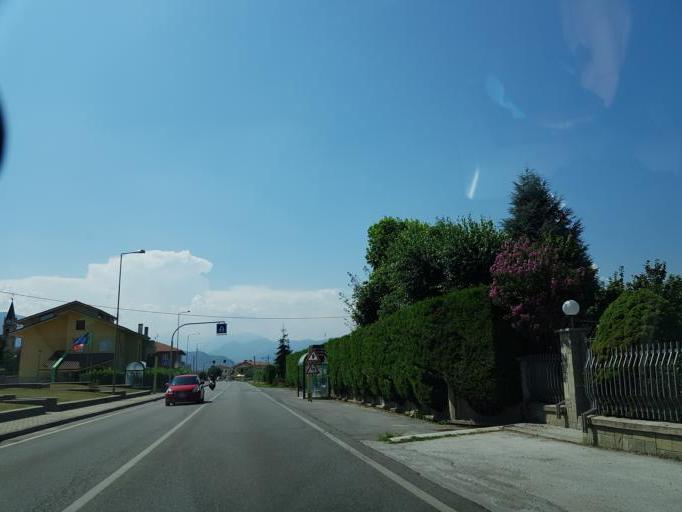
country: IT
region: Piedmont
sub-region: Provincia di Cuneo
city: San Rocco
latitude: 44.3976
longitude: 7.4773
